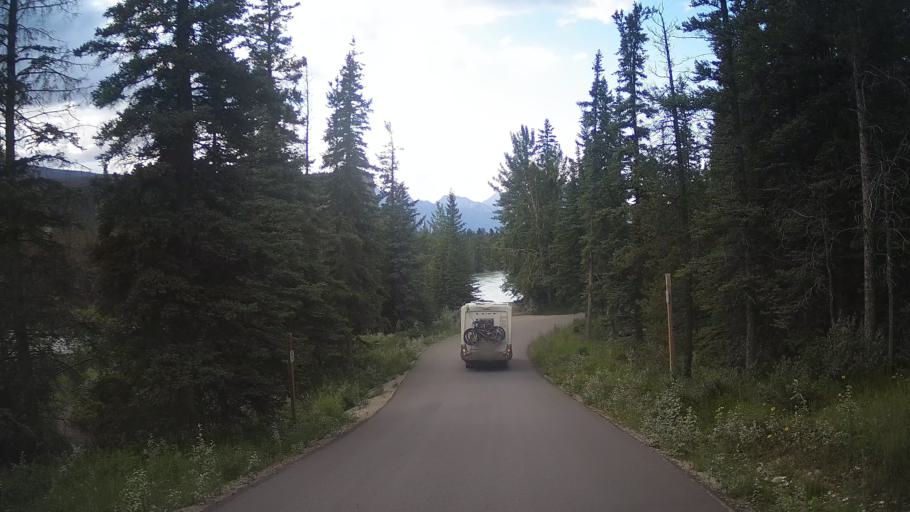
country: CA
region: Alberta
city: Jasper Park Lodge
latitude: 52.9318
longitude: -118.0325
